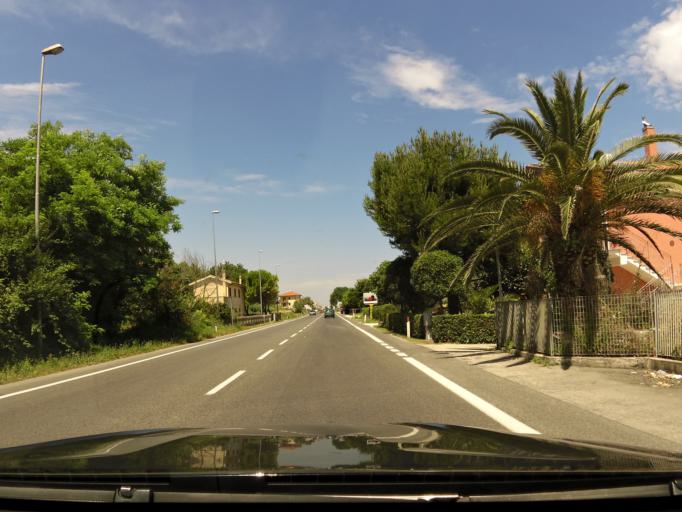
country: IT
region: The Marches
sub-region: Provincia di Pesaro e Urbino
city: Marotta
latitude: 43.7525
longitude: 13.1638
